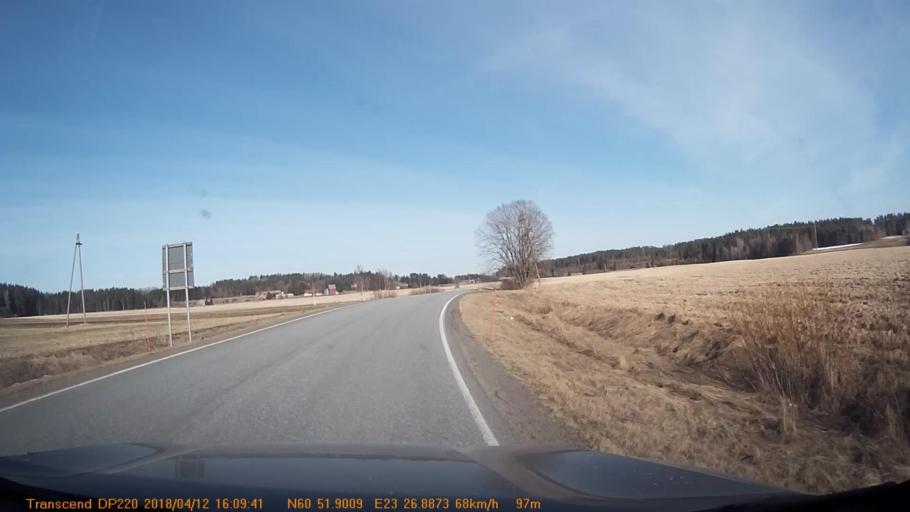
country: FI
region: Haeme
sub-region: Forssa
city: Jokioinen
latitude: 60.8651
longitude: 23.4485
